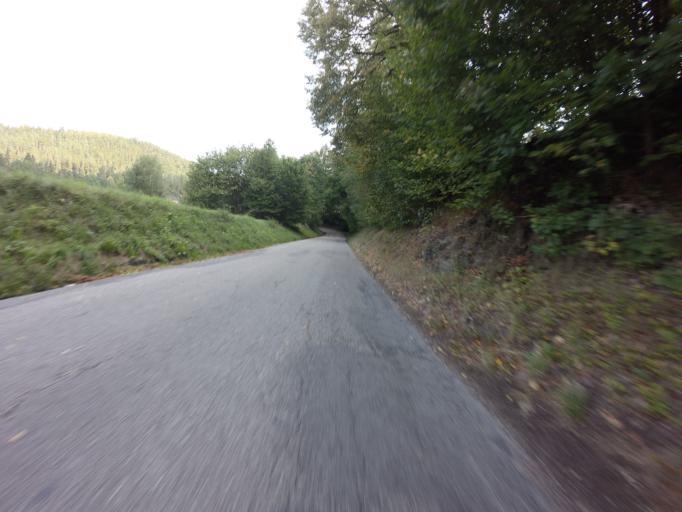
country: CZ
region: Jihocesky
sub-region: Okres Cesky Krumlov
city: Vyssi Brod
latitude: 48.6514
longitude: 14.3640
